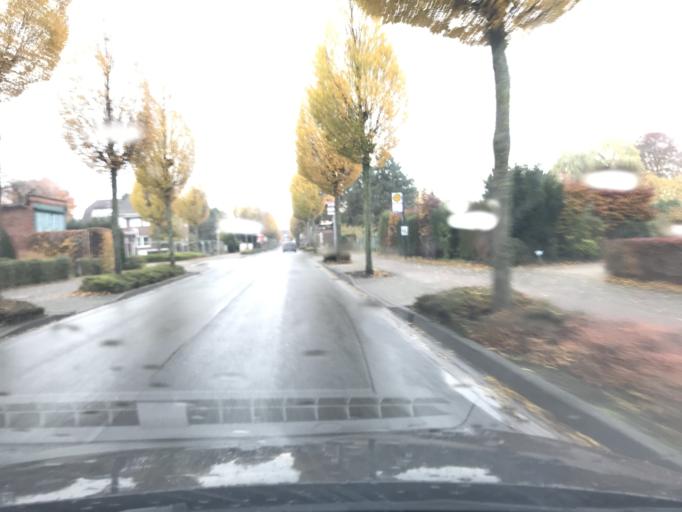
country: DE
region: North Rhine-Westphalia
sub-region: Regierungsbezirk Munster
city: Warendorf
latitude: 51.9210
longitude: 7.9593
